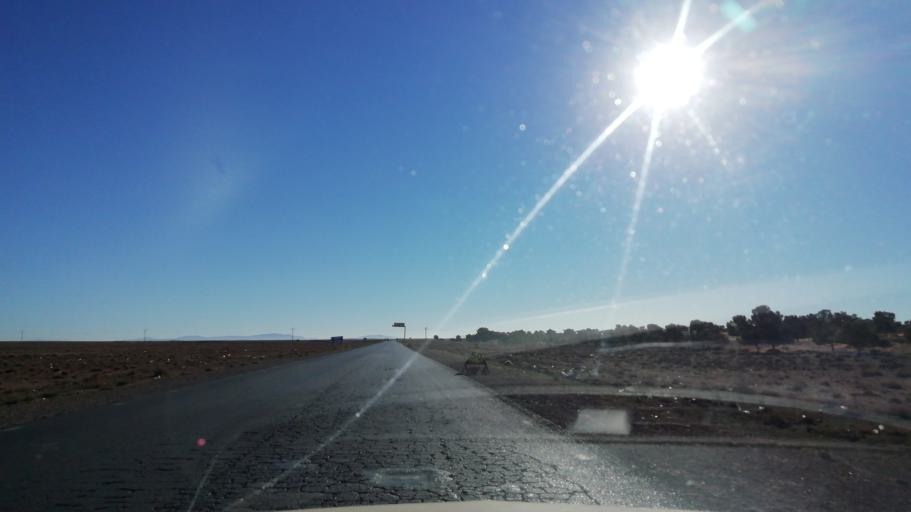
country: DZ
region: El Bayadh
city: El Bayadh
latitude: 33.8502
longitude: 0.6620
